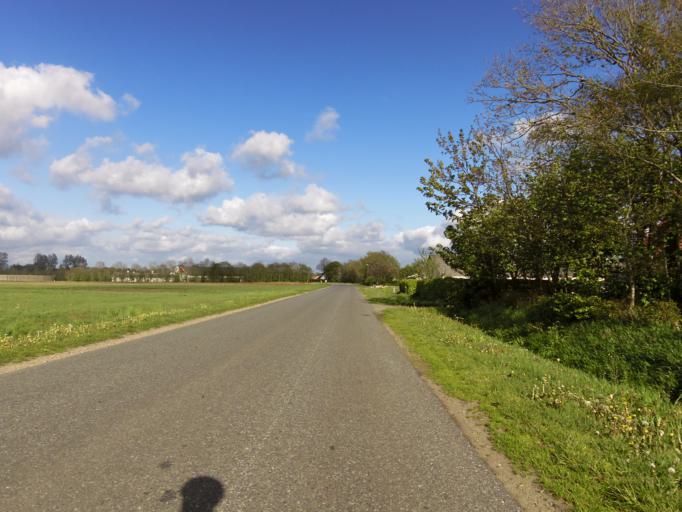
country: DK
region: South Denmark
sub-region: Esbjerg Kommune
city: Ribe
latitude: 55.2583
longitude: 8.8148
